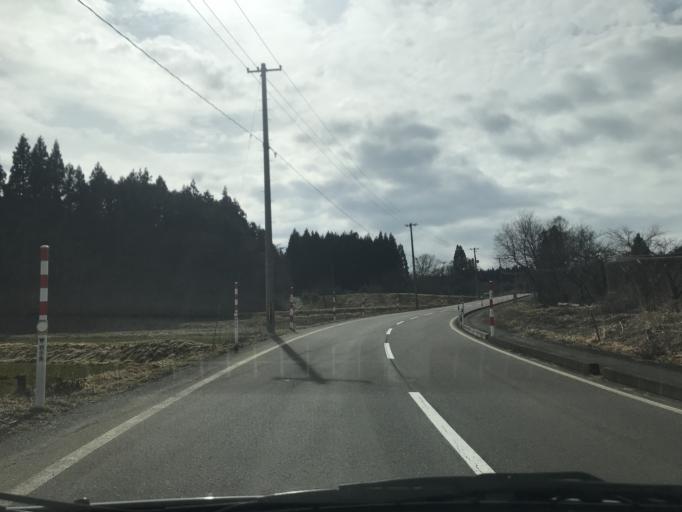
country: JP
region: Iwate
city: Hanamaki
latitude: 39.3924
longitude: 141.0269
